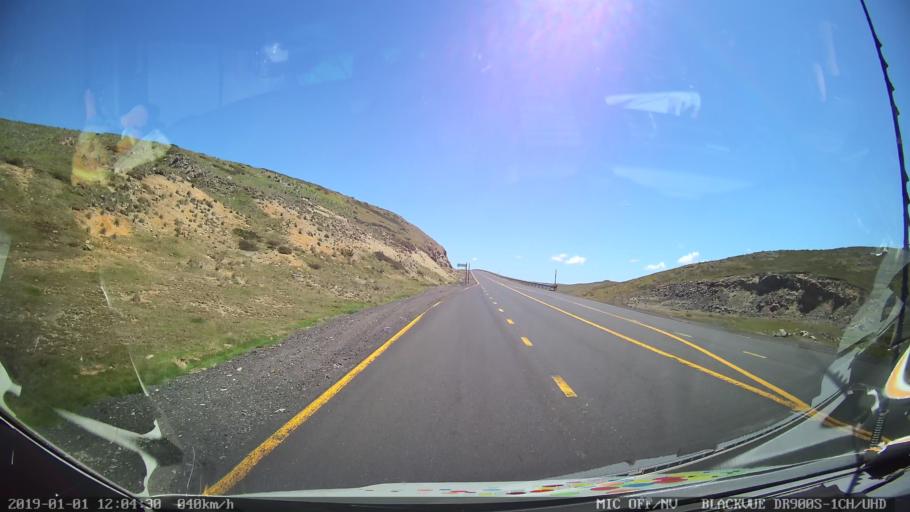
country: AU
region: New South Wales
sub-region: Snowy River
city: Jindabyne
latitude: -35.8664
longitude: 148.4971
